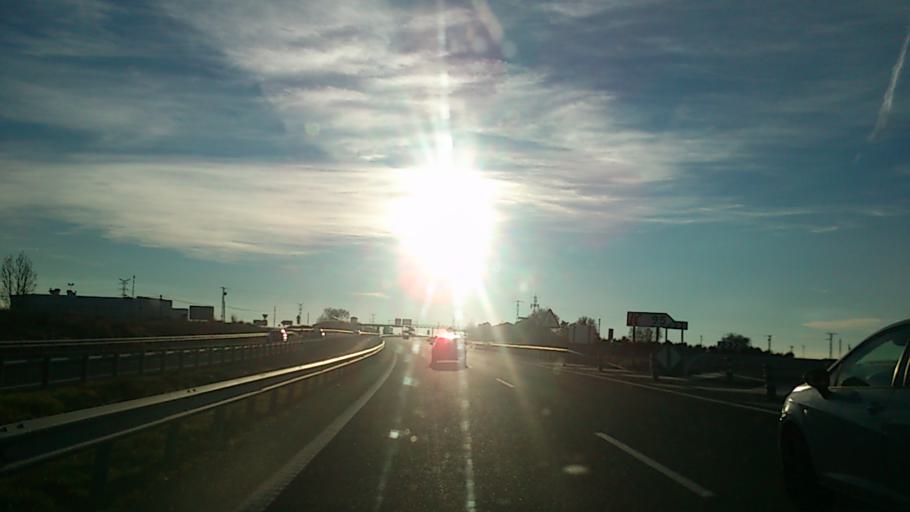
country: ES
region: Castille-La Mancha
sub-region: Provincia de Guadalajara
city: Ledanca
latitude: 40.8629
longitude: -2.8313
